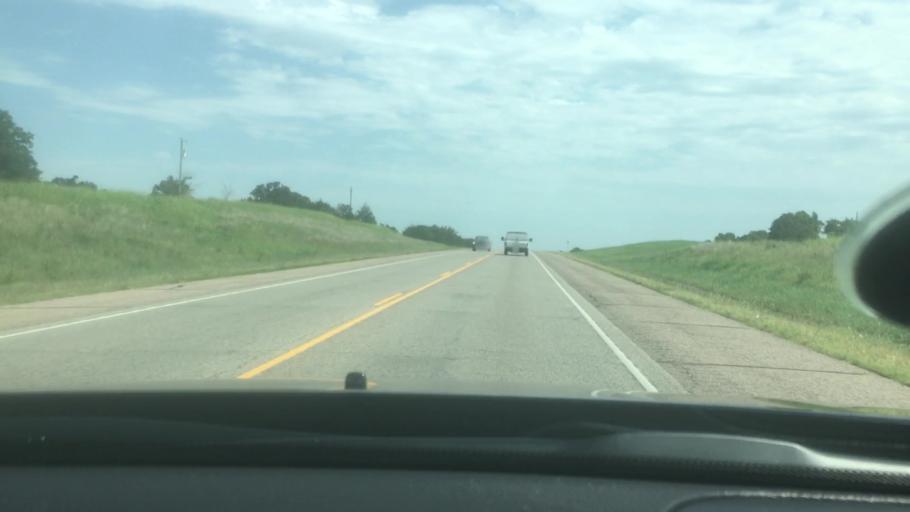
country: US
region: Oklahoma
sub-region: Seminole County
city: Maud
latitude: 35.0272
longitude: -96.9314
